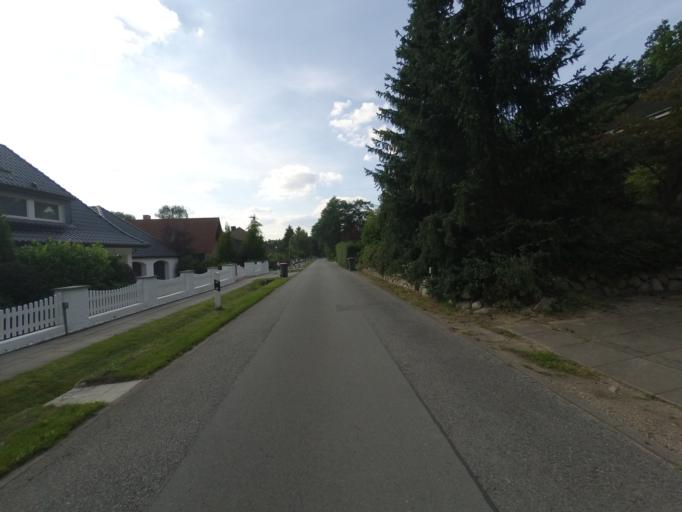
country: DE
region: Schleswig-Holstein
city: Oststeinbek
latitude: 53.5140
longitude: 10.1576
